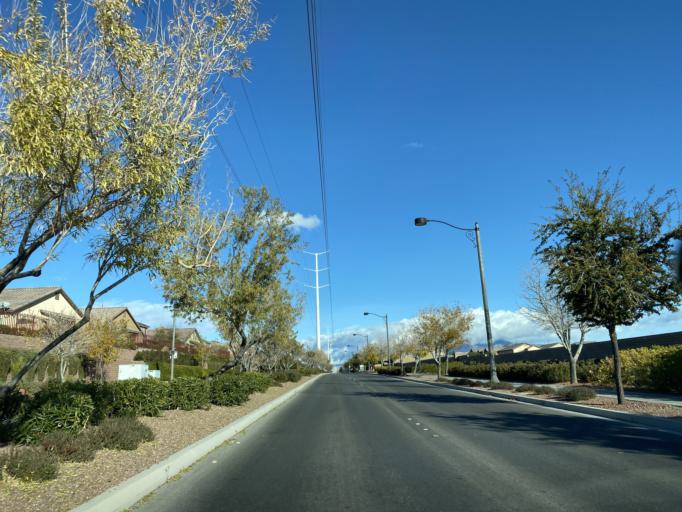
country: US
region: Nevada
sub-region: Clark County
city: Summerlin South
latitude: 36.2923
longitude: -115.3288
